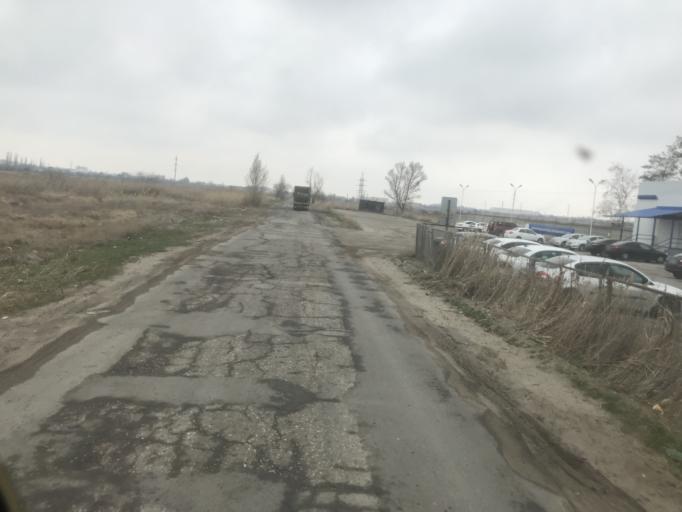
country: RU
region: Volgograd
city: Svetlyy Yar
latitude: 48.5157
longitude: 44.6312
